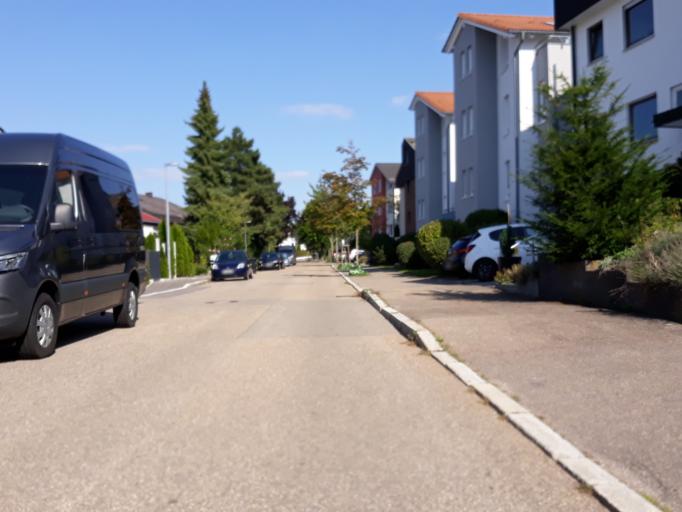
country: DE
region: Baden-Wuerttemberg
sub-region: Regierungsbezirk Stuttgart
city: Boeblingen
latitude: 48.6793
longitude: 9.0315
